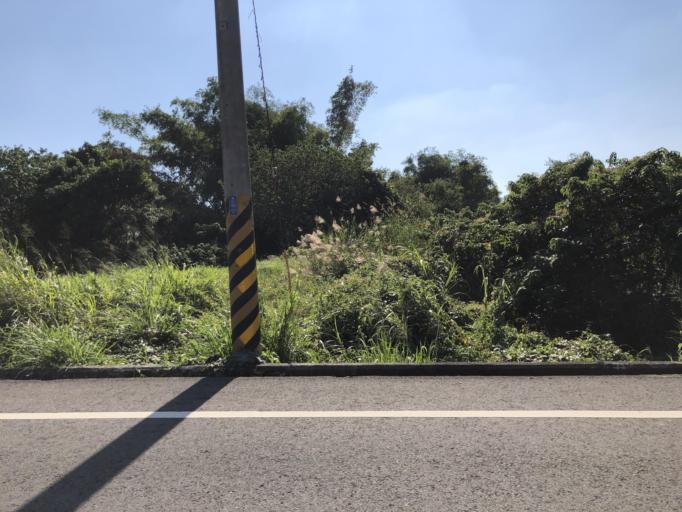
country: TW
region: Taiwan
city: Yujing
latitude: 23.0643
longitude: 120.3842
